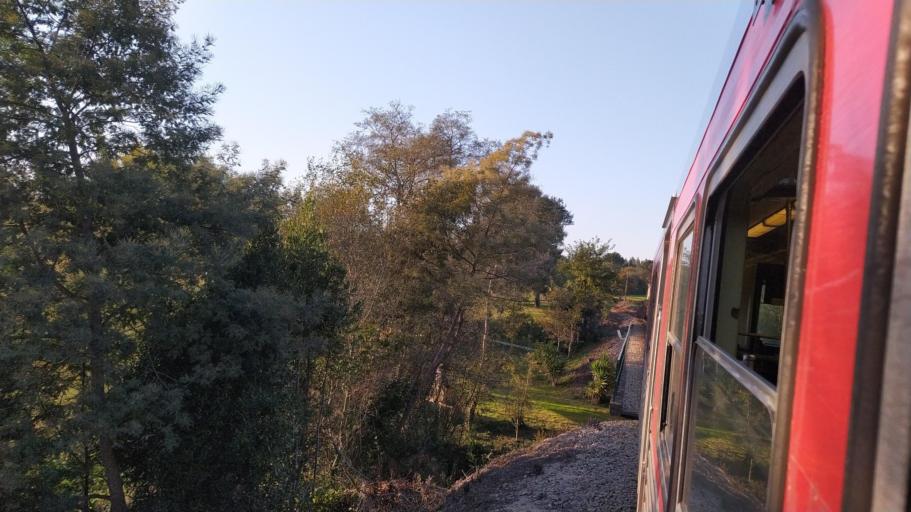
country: PT
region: Aveiro
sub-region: Aveiro
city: Eixo
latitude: 40.6361
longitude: -8.5805
